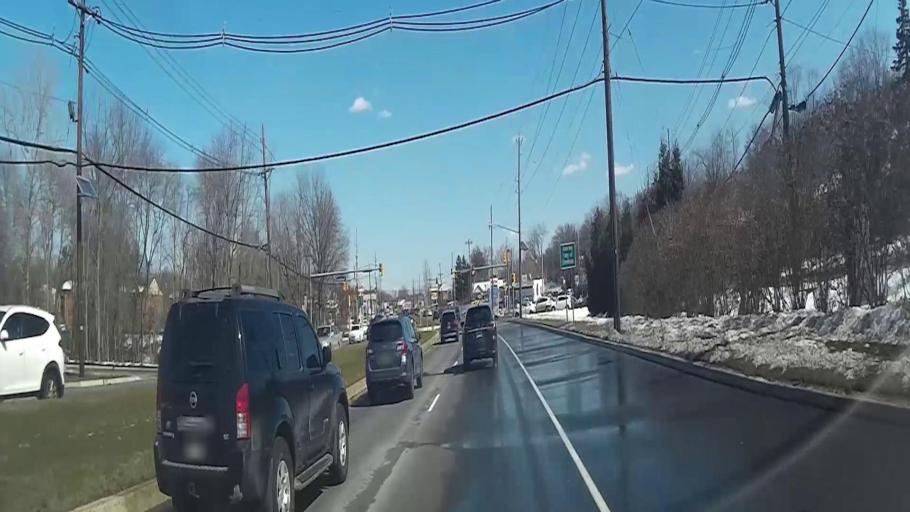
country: US
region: New Jersey
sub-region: Camden County
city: Greentree
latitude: 39.8958
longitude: -74.9466
